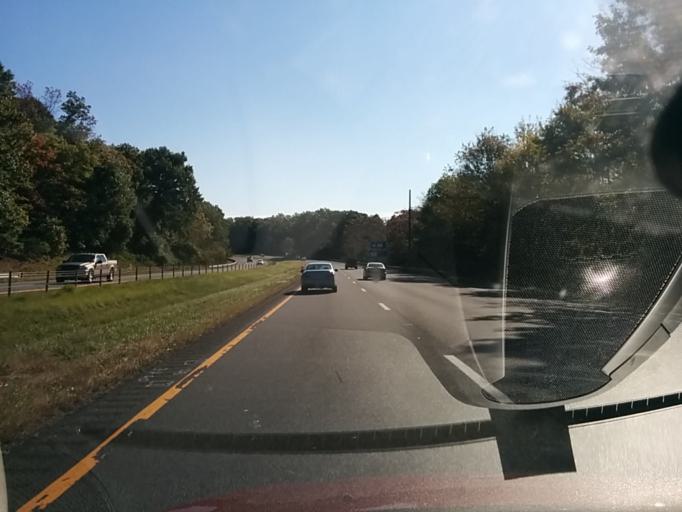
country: US
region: Virginia
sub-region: Albemarle County
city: Crozet
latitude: 38.0446
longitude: -78.7593
